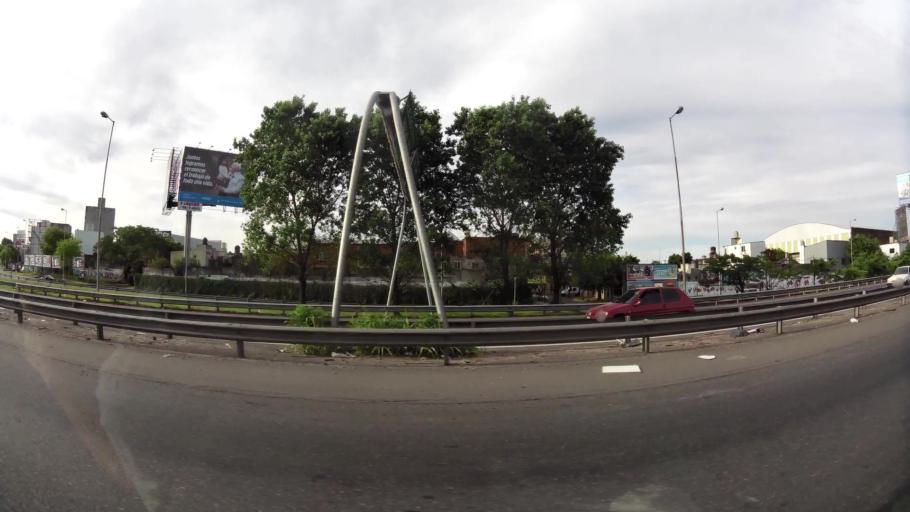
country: AR
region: Buenos Aires
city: Caseros
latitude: -34.6343
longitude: -58.5352
